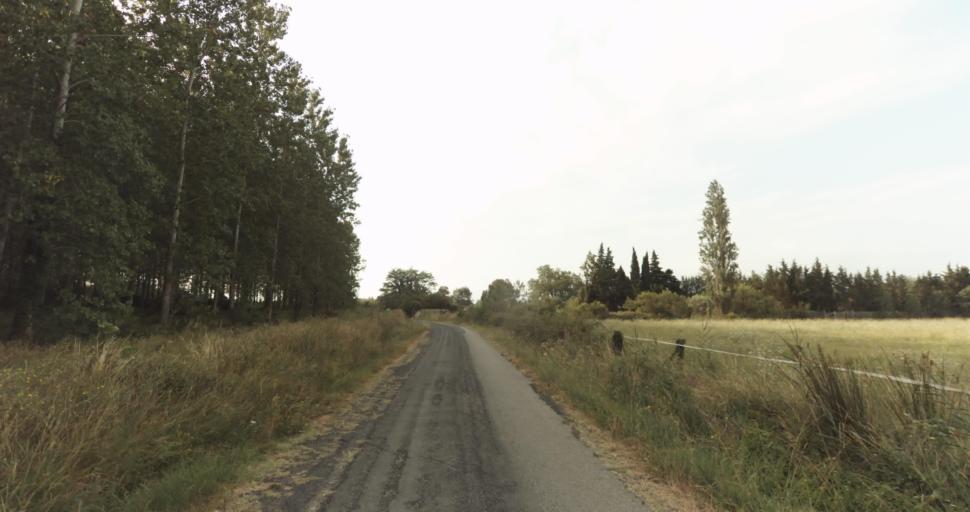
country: FR
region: Languedoc-Roussillon
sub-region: Departement des Pyrenees-Orientales
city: Corneilla-del-Vercol
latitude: 42.6279
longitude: 2.9420
